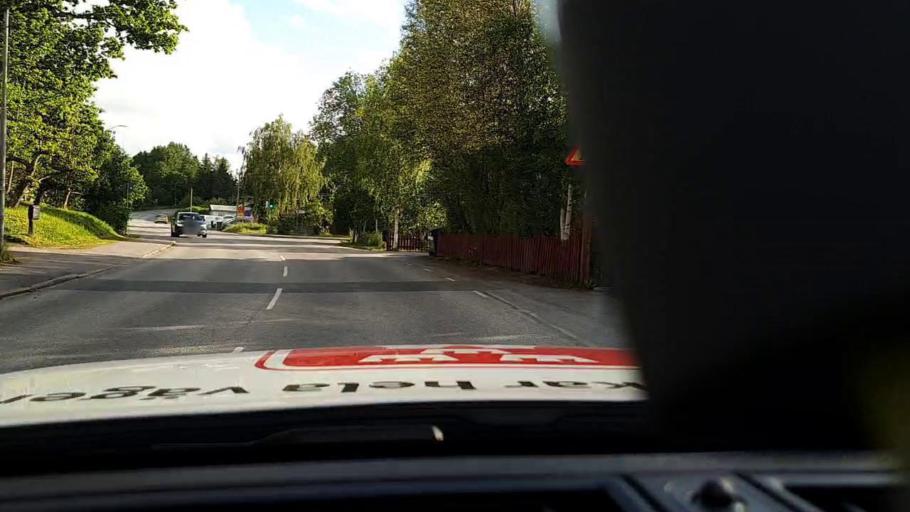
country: SE
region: Stockholm
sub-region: Huddinge Kommun
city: Huddinge
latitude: 59.2594
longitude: 17.9743
